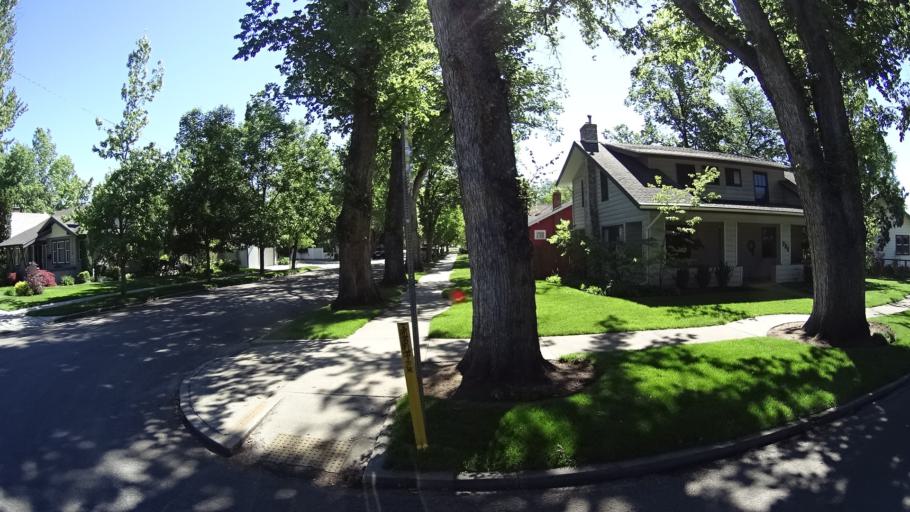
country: US
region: Idaho
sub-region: Ada County
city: Boise
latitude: 43.6265
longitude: -116.2109
